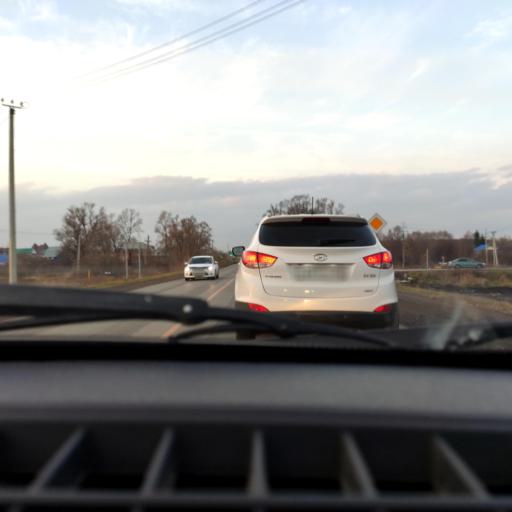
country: RU
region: Bashkortostan
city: Avdon
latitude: 54.7333
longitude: 55.8039
